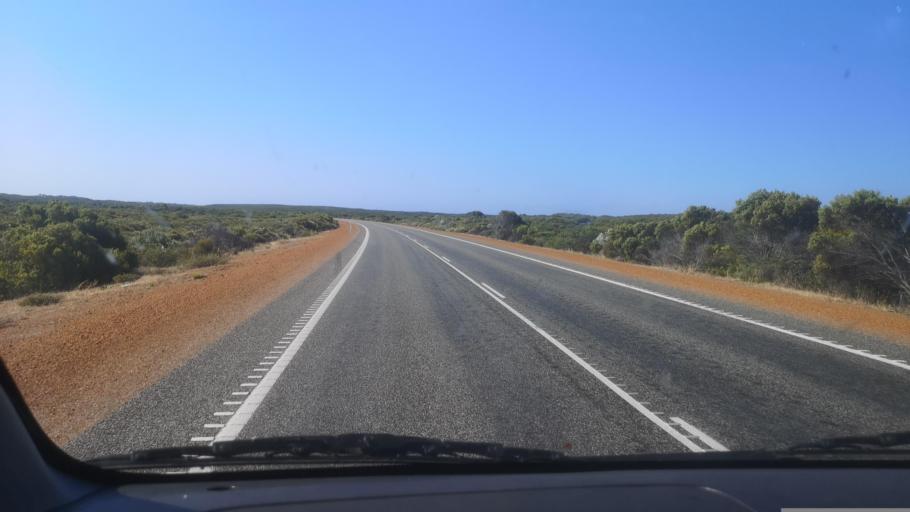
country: AU
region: Western Australia
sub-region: Dandaragan
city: Jurien Bay
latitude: -30.6363
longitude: 115.1343
